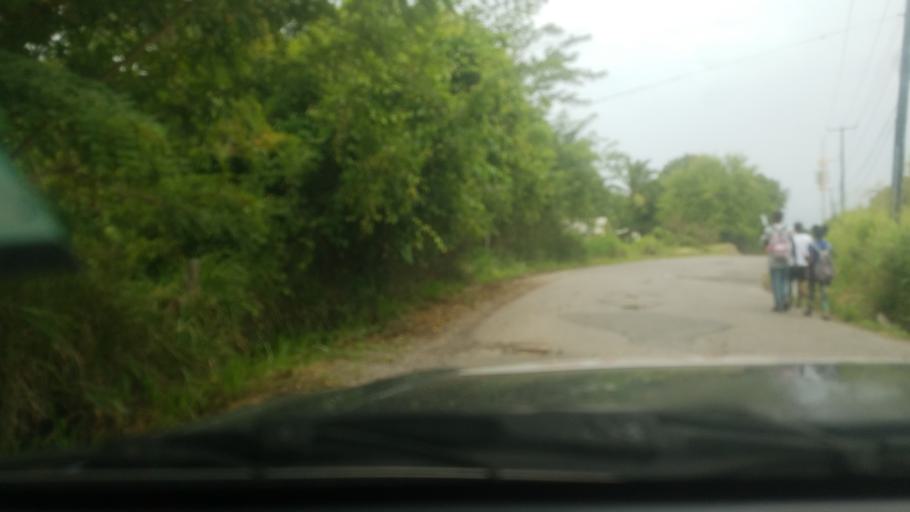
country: LC
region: Laborie Quarter
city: Laborie
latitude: 13.7527
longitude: -60.9802
